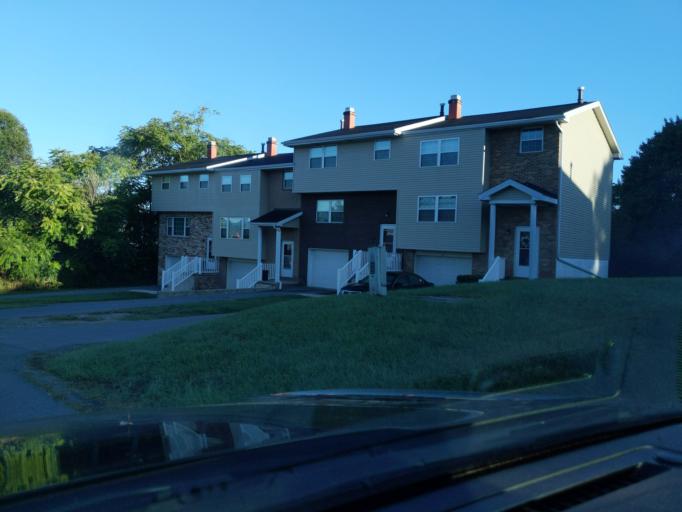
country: US
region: Pennsylvania
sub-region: Blair County
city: Greenwood
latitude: 40.5285
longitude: -78.3677
